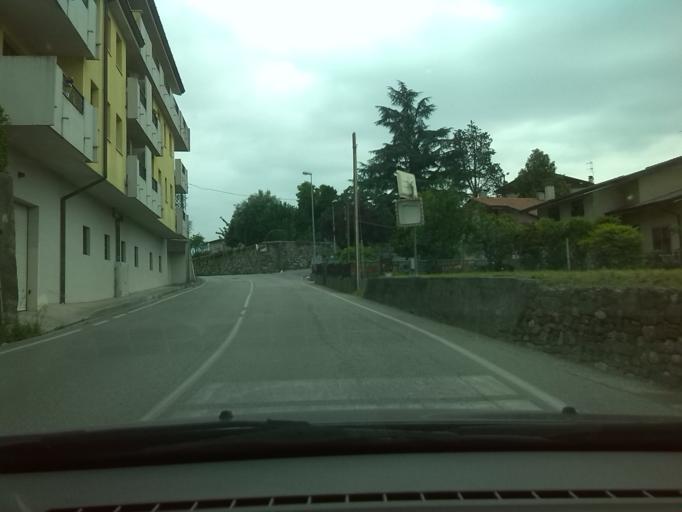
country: IT
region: Friuli Venezia Giulia
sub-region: Provincia di Udine
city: Santo Stefano
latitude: 46.2073
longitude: 13.1300
